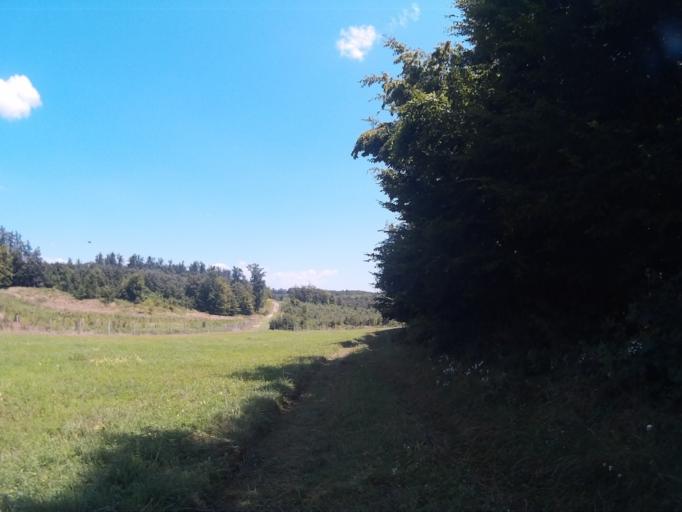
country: HU
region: Veszprem
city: Zirc
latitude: 47.2050
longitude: 17.8965
